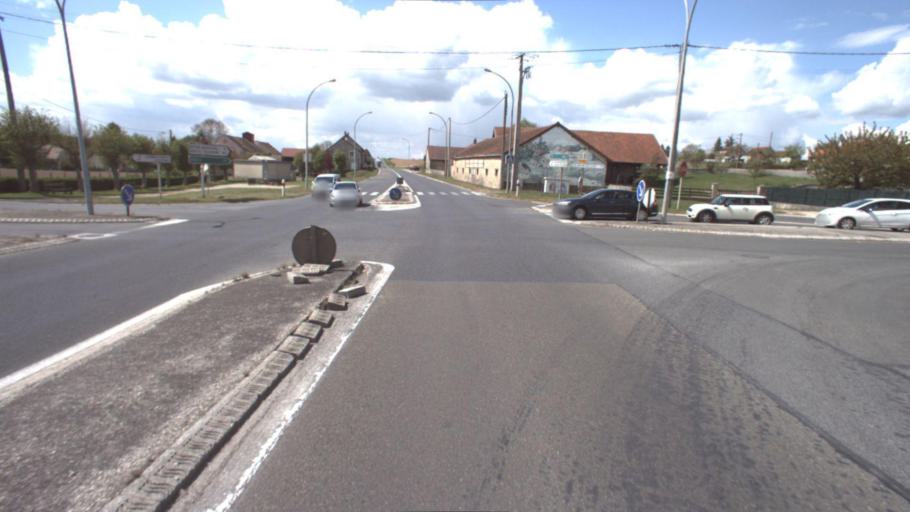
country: FR
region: Ile-de-France
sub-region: Departement de Seine-et-Marne
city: La Ferte-Gaucher
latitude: 48.6971
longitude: 3.2927
